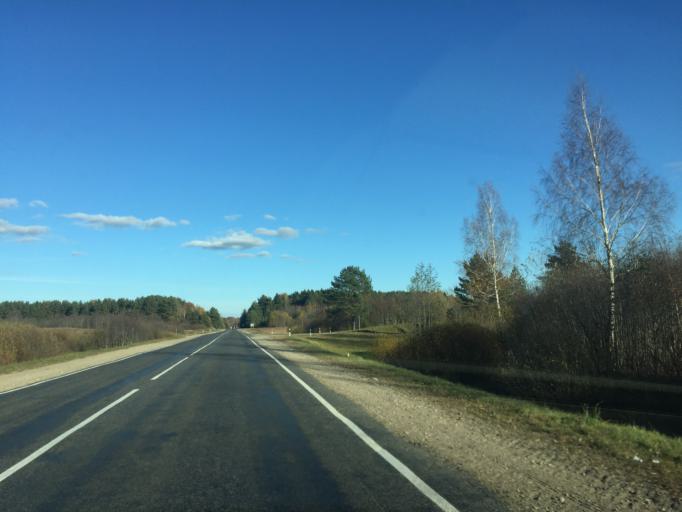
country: BY
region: Vitebsk
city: Dzisna
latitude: 55.2451
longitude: 28.0839
